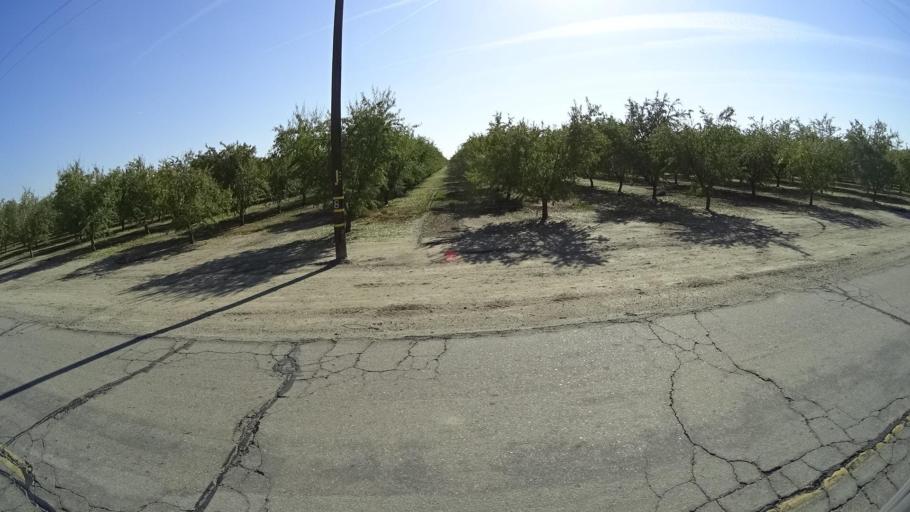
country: US
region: California
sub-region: Kern County
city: Wasco
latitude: 35.6670
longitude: -119.3729
